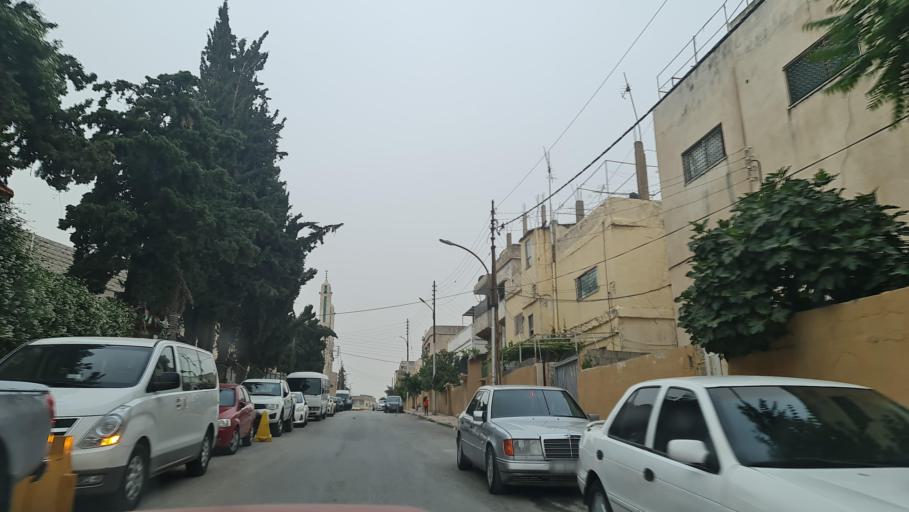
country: JO
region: Amman
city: Amman
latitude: 31.9358
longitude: 35.9350
